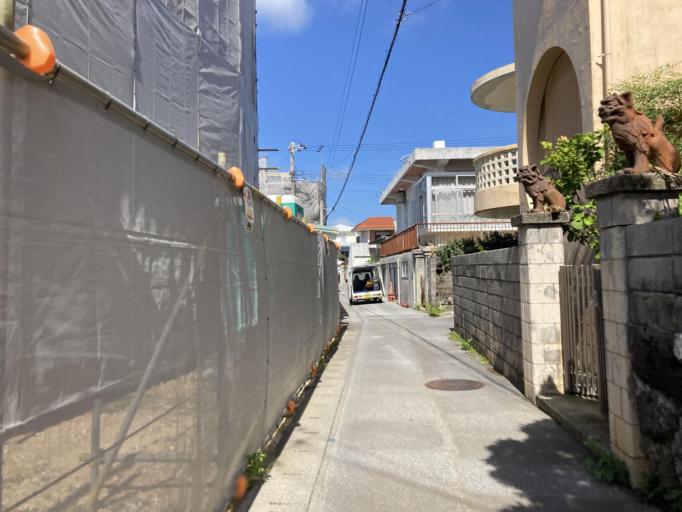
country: JP
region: Okinawa
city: Itoman
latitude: 26.1286
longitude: 127.7713
